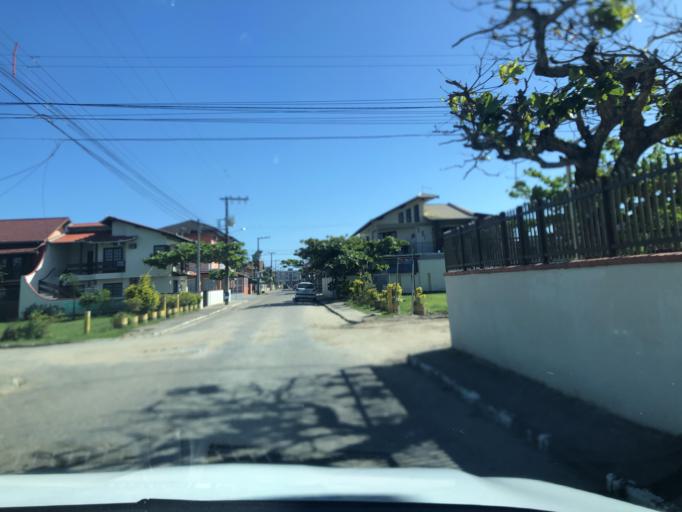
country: BR
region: Santa Catarina
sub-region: Sao Francisco Do Sul
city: Sao Francisco do Sul
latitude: -26.2289
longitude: -48.5103
